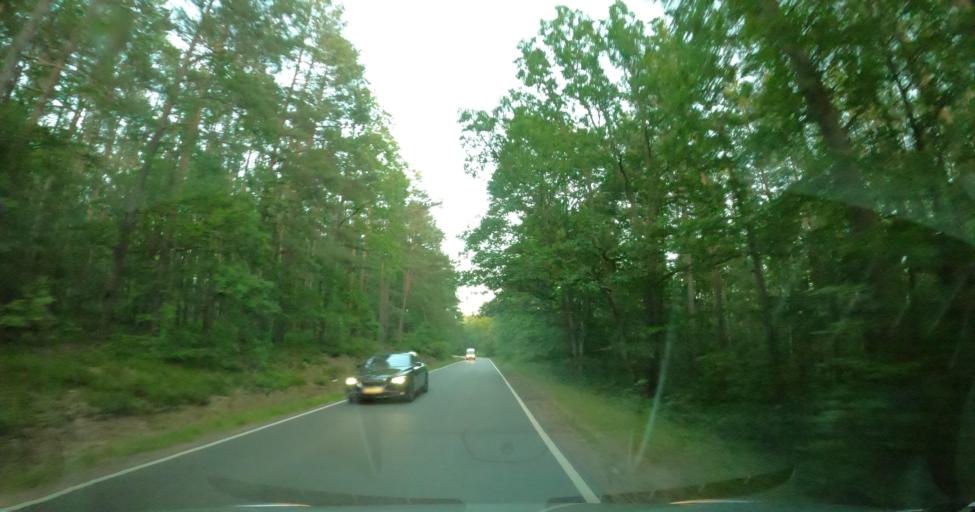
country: PL
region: Pomeranian Voivodeship
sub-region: Powiat leborski
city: Lebork
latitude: 54.5015
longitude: 17.8228
